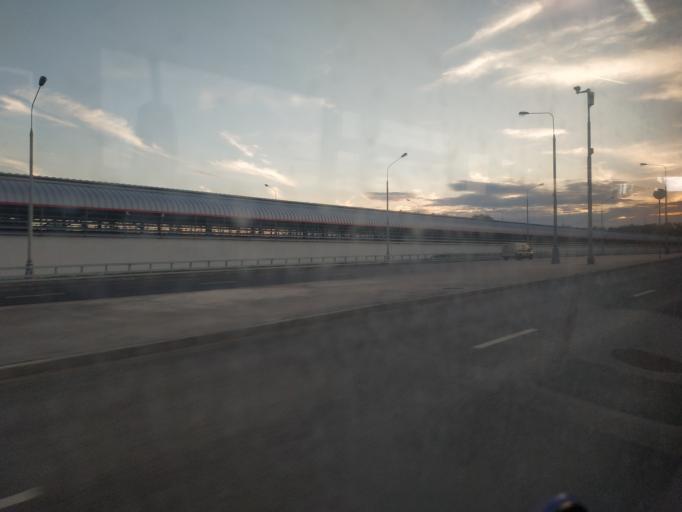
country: RU
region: Moskovskaya
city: Mosrentgen
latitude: 55.5896
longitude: 37.4269
